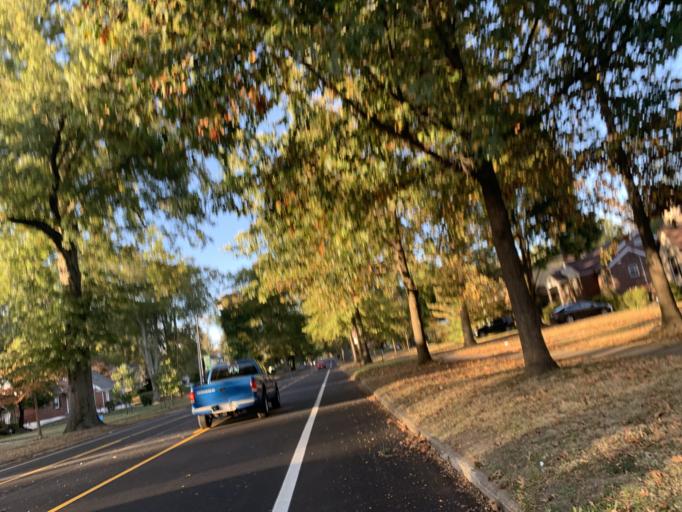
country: US
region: Indiana
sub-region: Floyd County
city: New Albany
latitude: 38.2467
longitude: -85.8297
